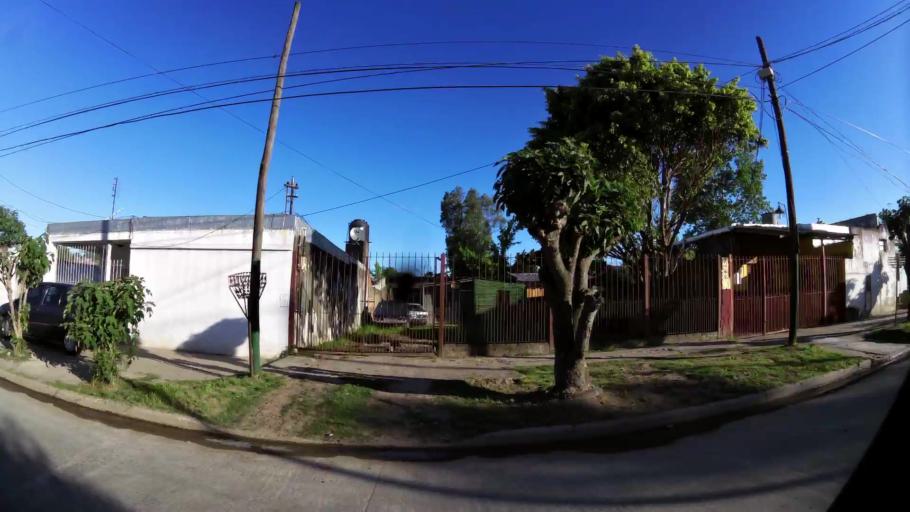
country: AR
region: Buenos Aires
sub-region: Partido de Almirante Brown
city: Adrogue
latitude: -34.7676
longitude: -58.3354
